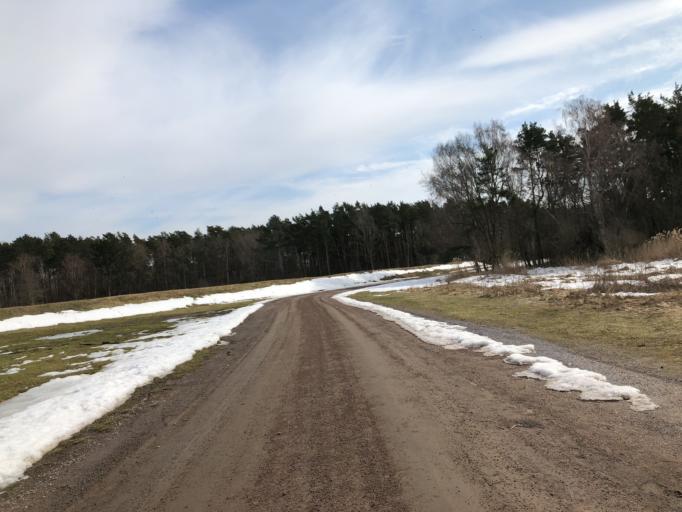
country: SE
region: Kalmar
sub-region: Kalmar Kommun
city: Kalmar
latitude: 56.6607
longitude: 16.3164
